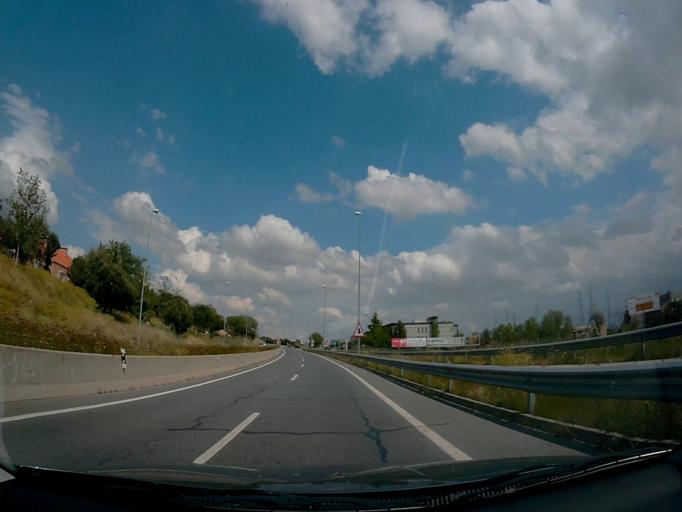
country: ES
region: Madrid
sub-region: Provincia de Madrid
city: Villaviciosa de Odon
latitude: 40.3514
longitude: -3.9084
